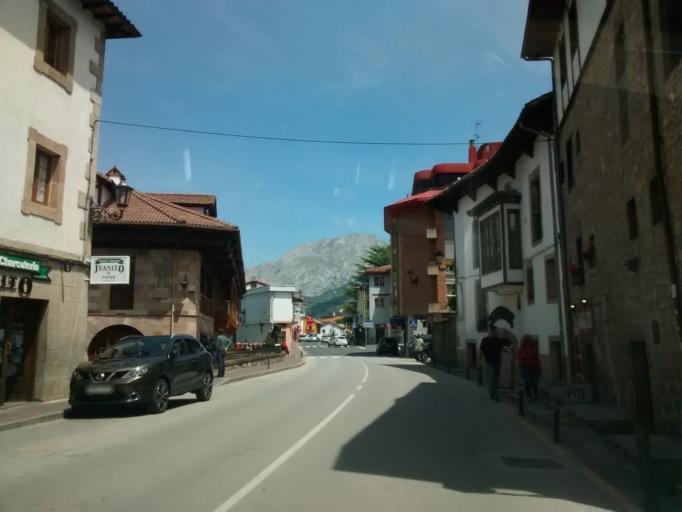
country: ES
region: Cantabria
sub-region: Provincia de Cantabria
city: Potes
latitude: 43.1545
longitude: -4.6210
